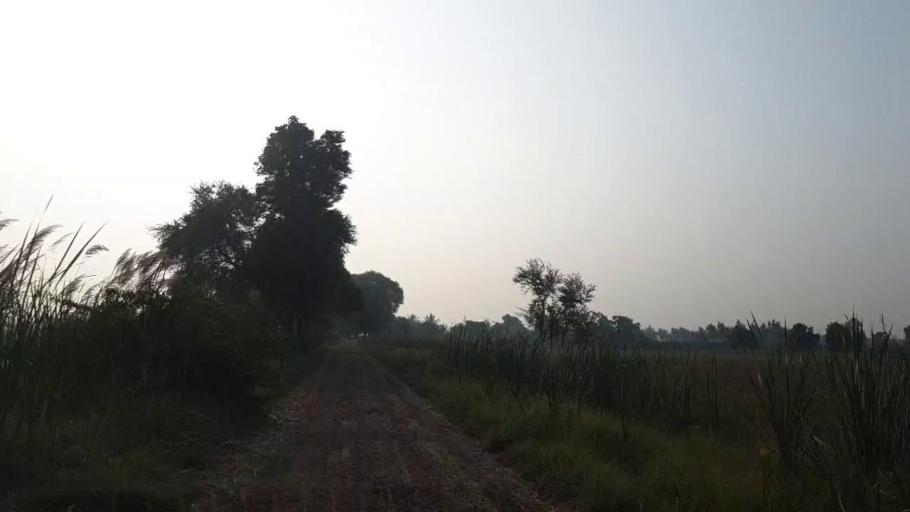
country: PK
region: Sindh
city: Tando Muhammad Khan
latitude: 25.1214
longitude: 68.5642
